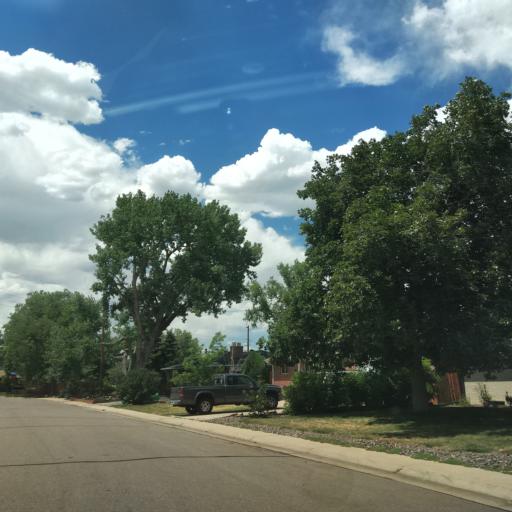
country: US
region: Colorado
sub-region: Jefferson County
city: Lakewood
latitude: 39.6882
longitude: -105.0966
